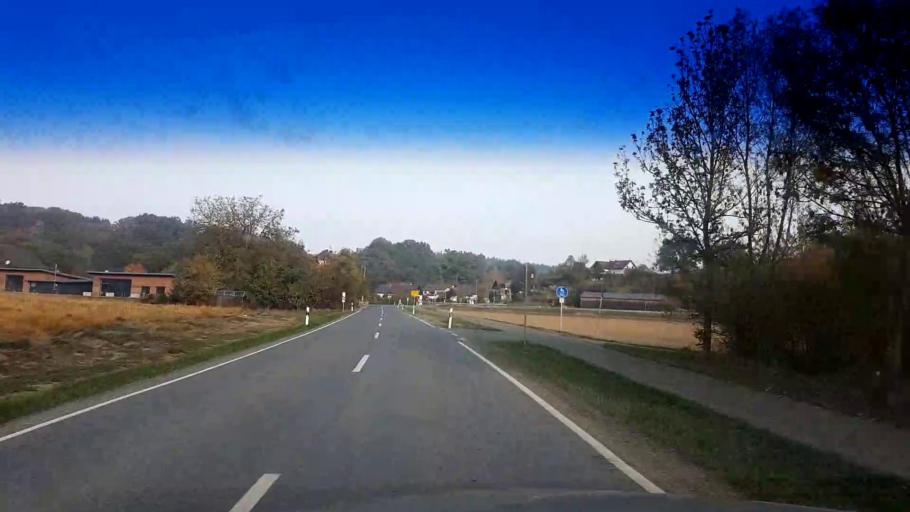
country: DE
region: Bavaria
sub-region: Upper Franconia
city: Altenkunstadt
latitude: 50.1231
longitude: 11.3000
